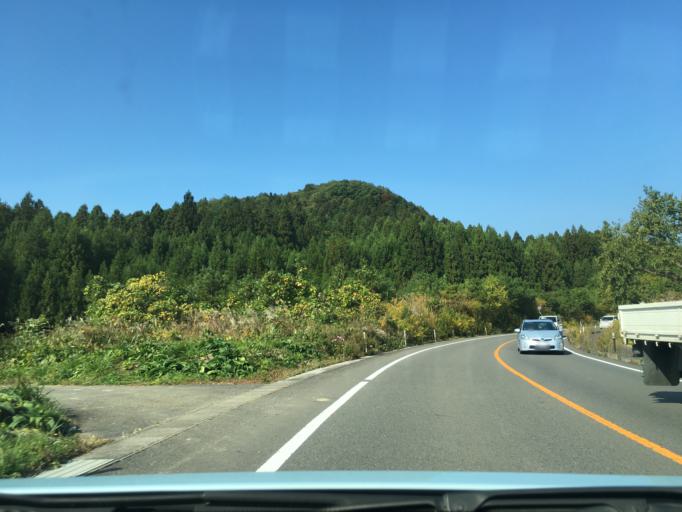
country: JP
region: Fukushima
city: Sukagawa
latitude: 37.2893
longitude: 140.1669
